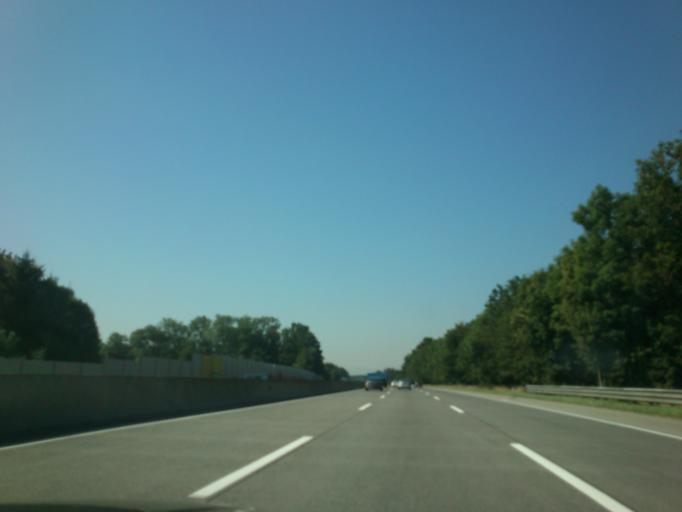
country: AT
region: Upper Austria
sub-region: Politischer Bezirk Linz-Land
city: Horsching
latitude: 48.1712
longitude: 14.1719
